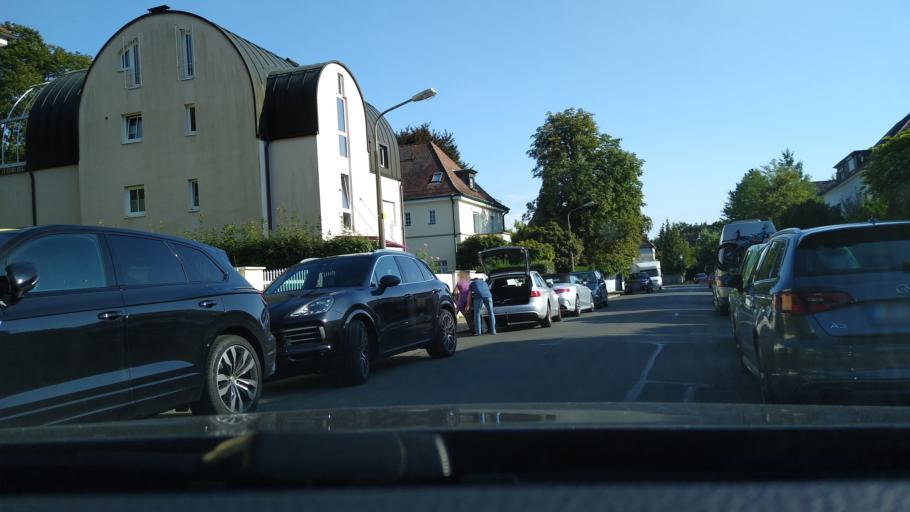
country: DE
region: Bavaria
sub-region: Regierungsbezirk Mittelfranken
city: Nuernberg
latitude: 49.4334
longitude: 11.1000
